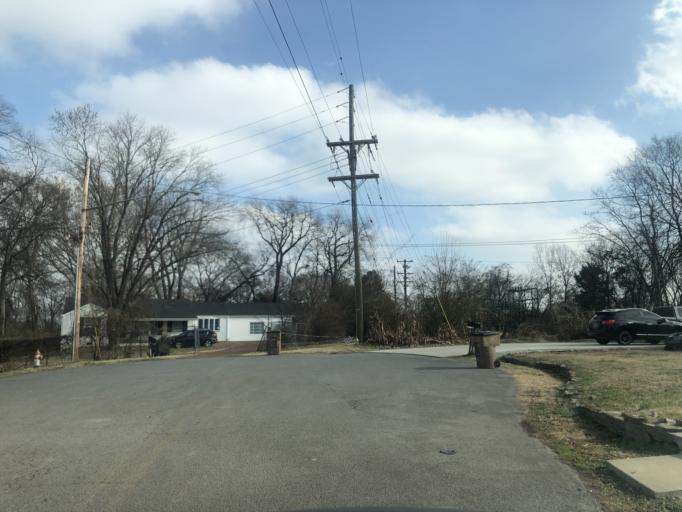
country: US
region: Tennessee
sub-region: Davidson County
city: Oak Hill
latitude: 36.0979
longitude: -86.7178
